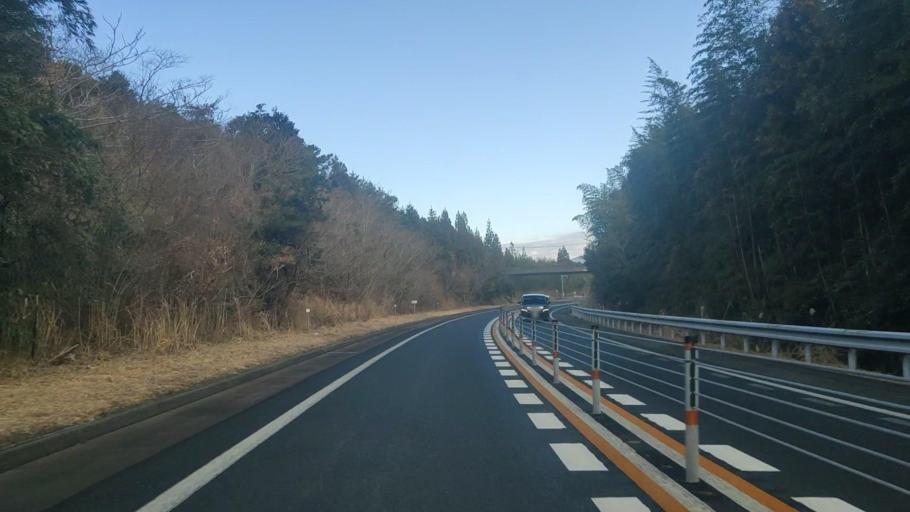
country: JP
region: Oita
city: Hiji
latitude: 33.3980
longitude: 131.4301
